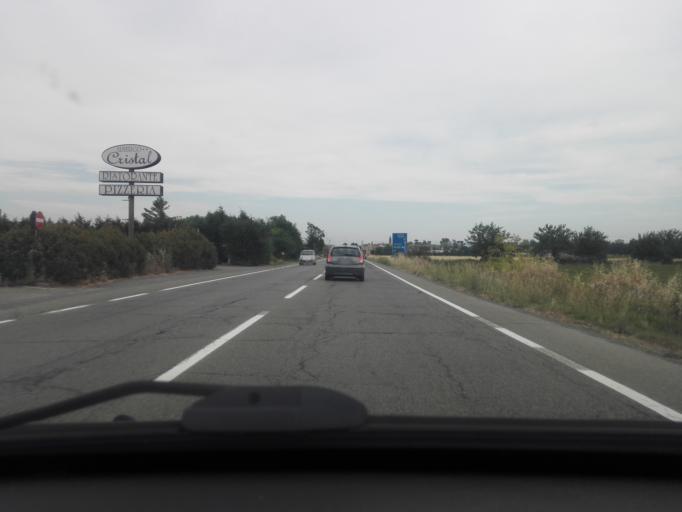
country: IT
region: Piedmont
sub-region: Provincia di Alessandria
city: Pozzolo Formigaro
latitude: 44.8028
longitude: 8.7737
